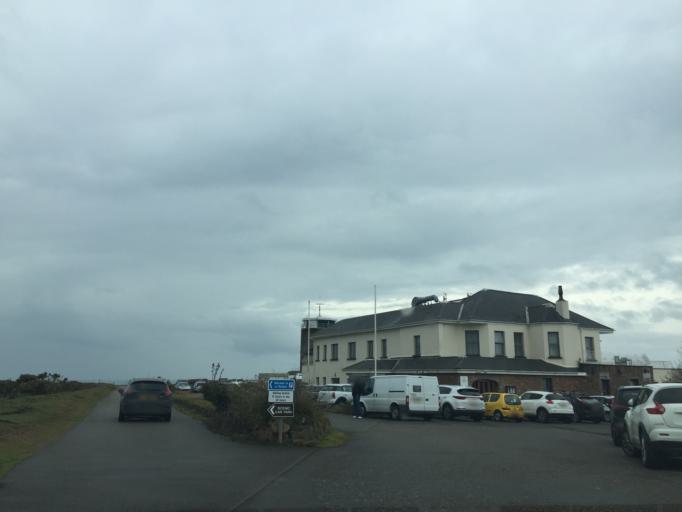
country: JE
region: St Helier
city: Saint Helier
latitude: 49.1811
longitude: -2.2385
